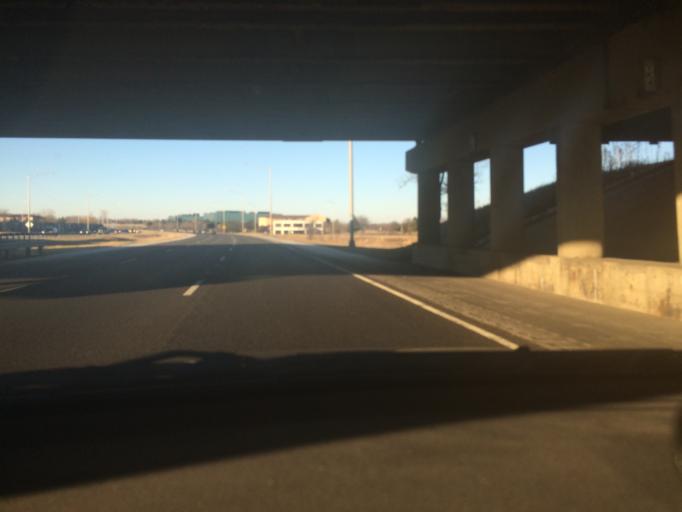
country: US
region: Illinois
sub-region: Lake County
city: Long Grove
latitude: 42.1389
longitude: -88.0048
